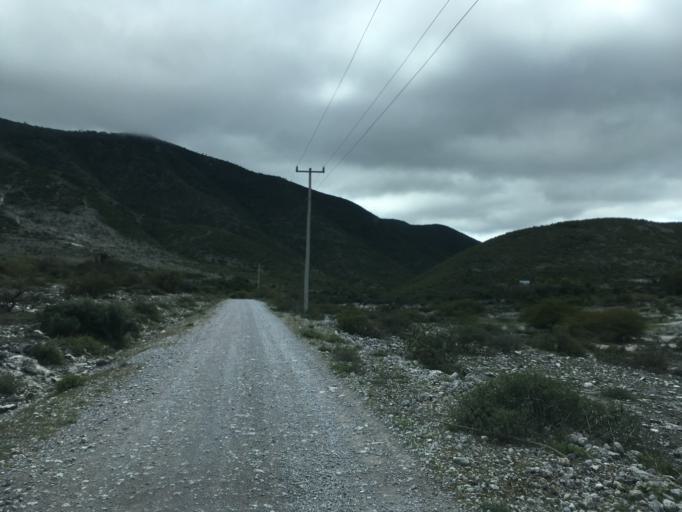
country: MX
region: Hidalgo
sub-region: Metztitlan
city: Fontezuelas
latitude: 20.6287
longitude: -98.8594
